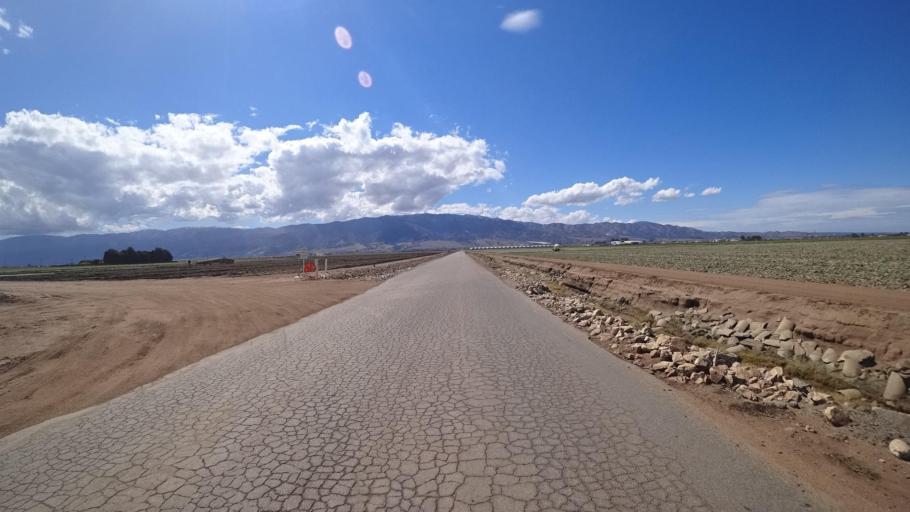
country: US
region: California
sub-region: Monterey County
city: Chualar
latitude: 36.5976
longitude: -121.5252
